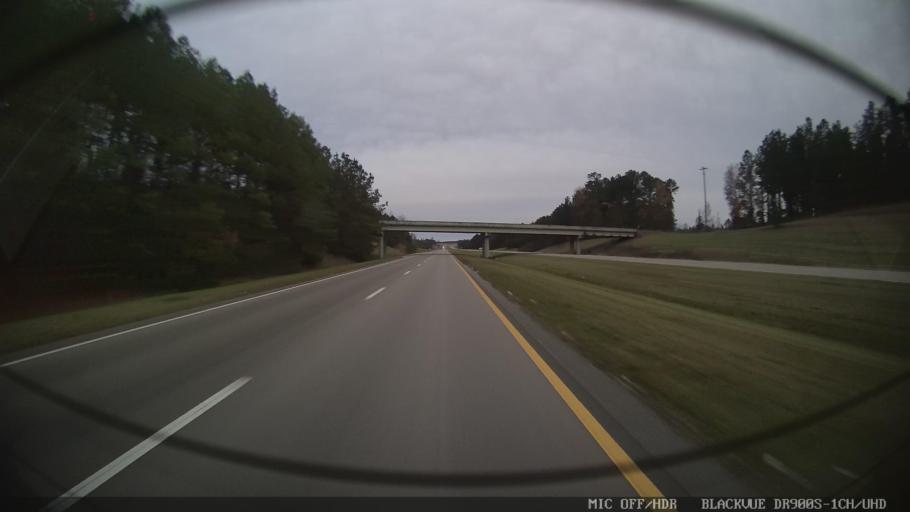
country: US
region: Mississippi
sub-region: Clarke County
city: Quitman
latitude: 32.0779
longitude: -88.6900
